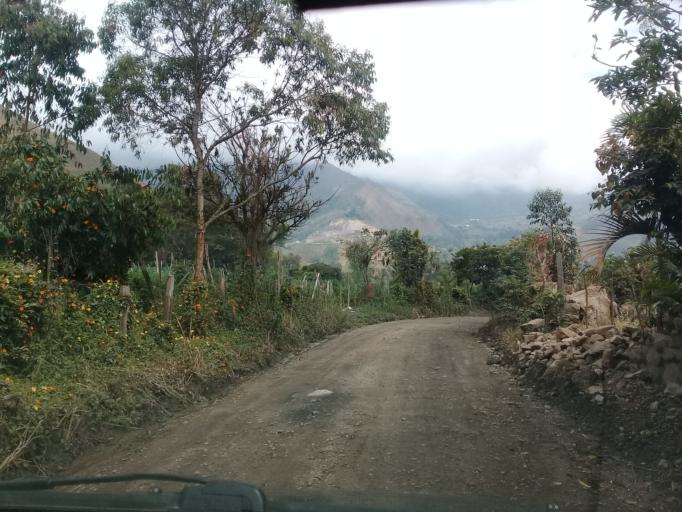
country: CO
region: Cundinamarca
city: Une
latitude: 4.4085
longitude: -73.9910
